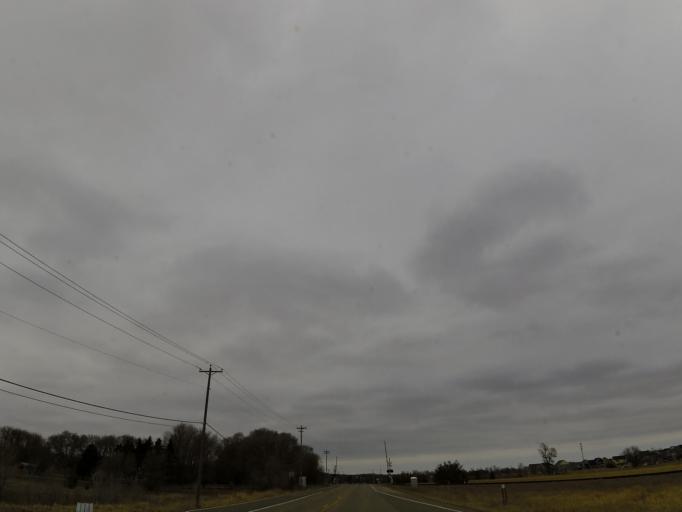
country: US
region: Minnesota
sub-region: Washington County
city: Bayport
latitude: 45.0071
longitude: -92.7943
